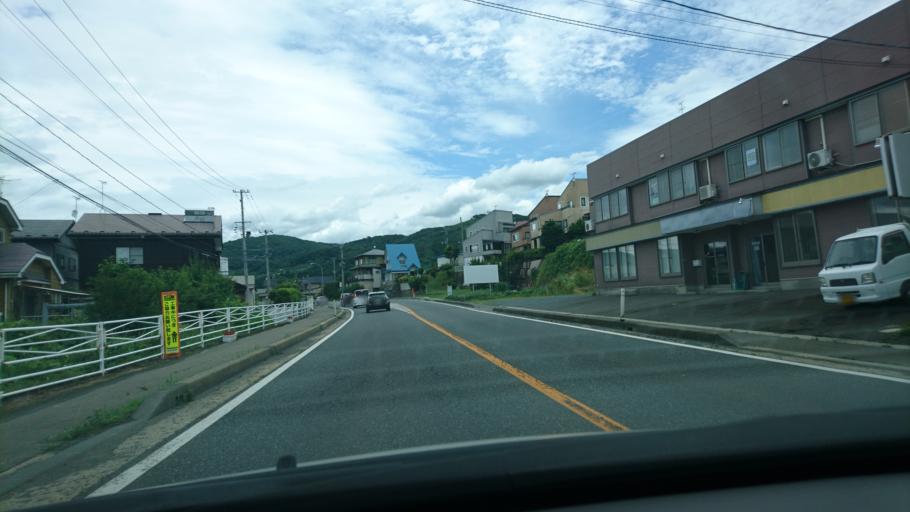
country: JP
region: Iwate
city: Morioka-shi
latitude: 39.6362
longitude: 141.1854
